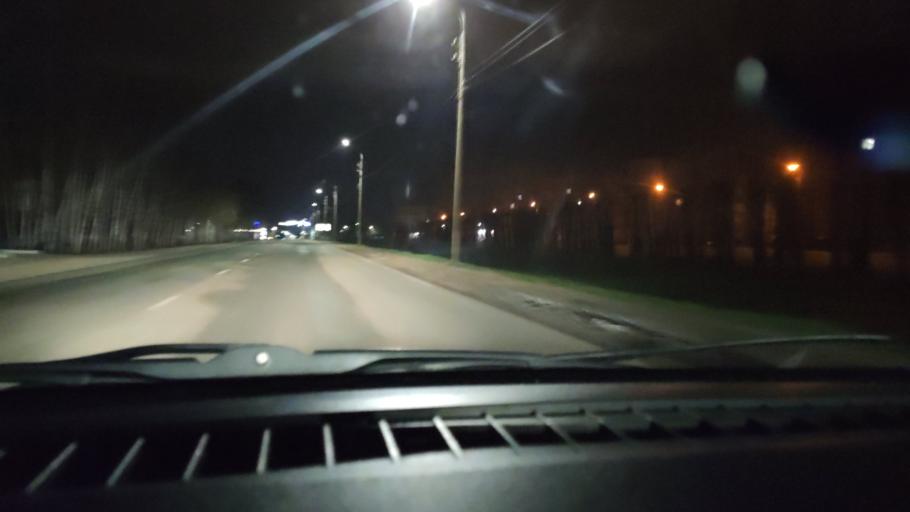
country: RU
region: Bashkortostan
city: Sterlitamak
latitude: 53.6407
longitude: 55.9013
